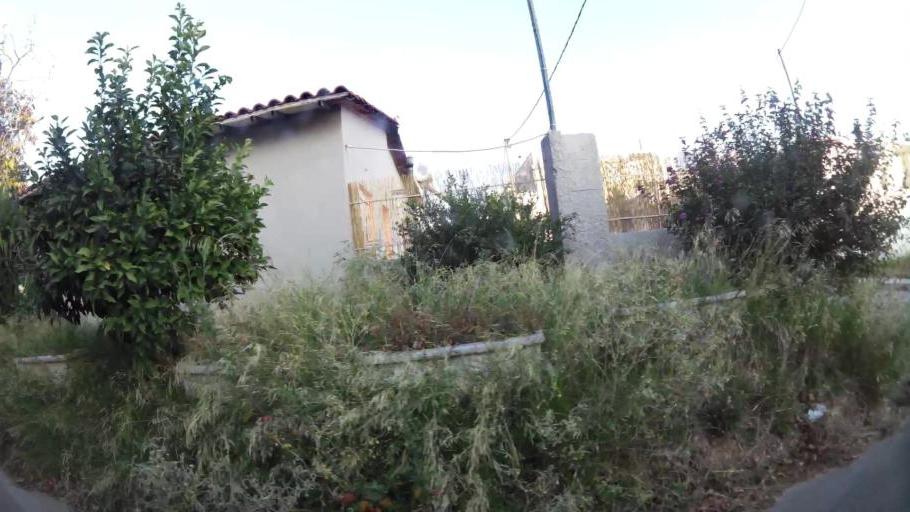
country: GR
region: Attica
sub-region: Nomarchia Anatolikis Attikis
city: Acharnes
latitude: 38.0955
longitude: 23.7401
